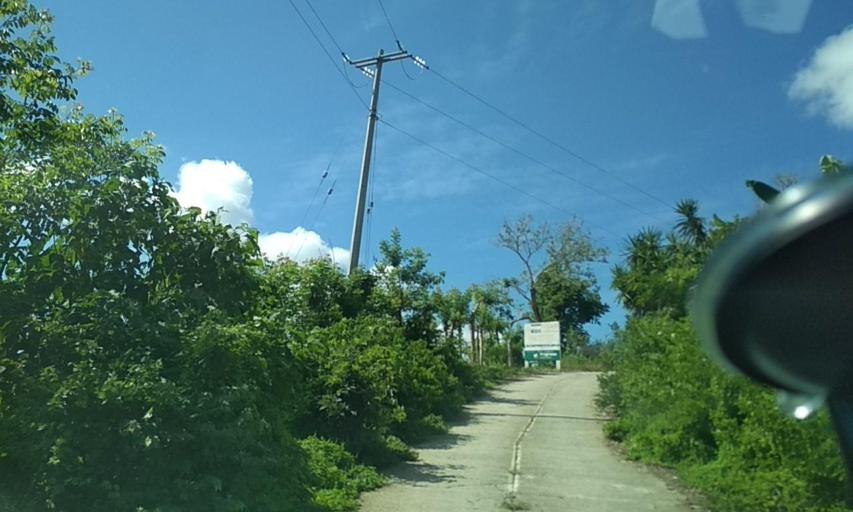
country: MX
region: Veracruz
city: Cazones de Herrera
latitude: 20.6217
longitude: -97.3234
